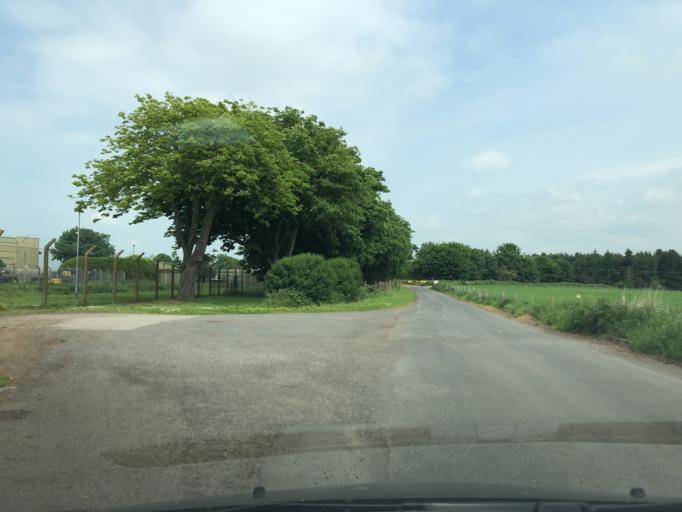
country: GB
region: England
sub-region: North Yorkshire
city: Boroughbridge
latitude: 54.1375
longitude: -1.4083
